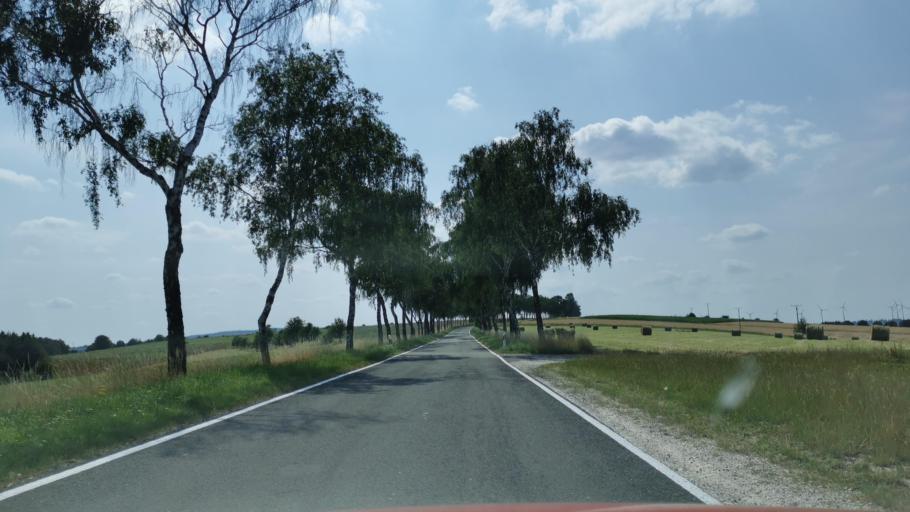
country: DE
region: Rheinland-Pfalz
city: Talling
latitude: 49.7597
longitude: 6.9348
